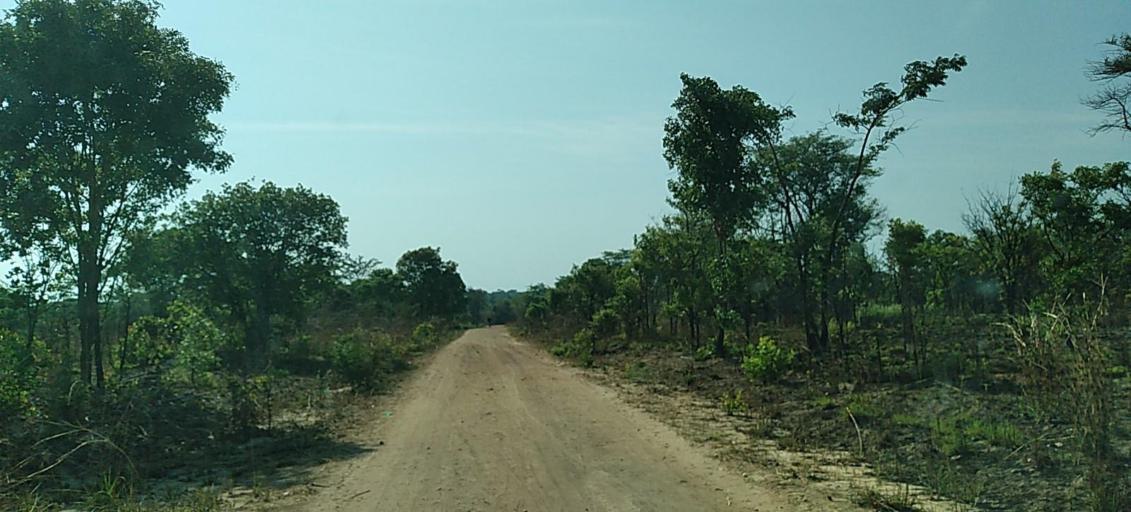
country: ZM
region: Copperbelt
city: Luanshya
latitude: -13.1889
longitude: 28.4745
